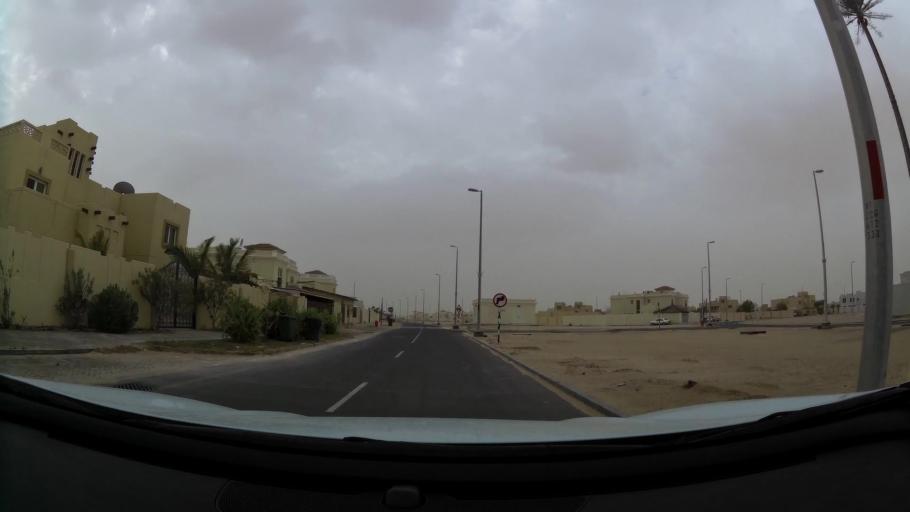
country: AE
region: Abu Dhabi
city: Abu Dhabi
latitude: 24.4458
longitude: 54.7182
